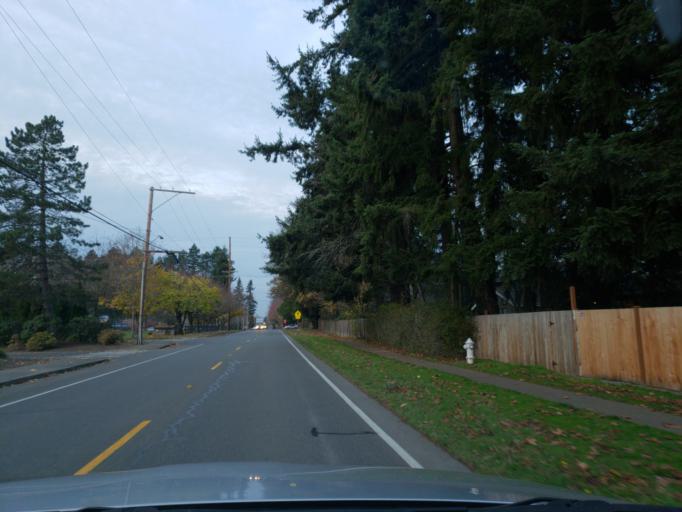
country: US
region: Washington
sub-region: King County
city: Bothell
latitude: 47.7685
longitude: -122.2232
